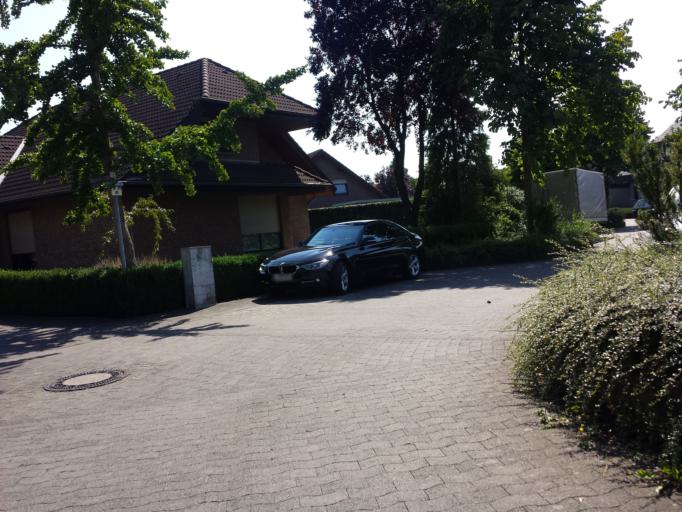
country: DE
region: North Rhine-Westphalia
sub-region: Regierungsbezirk Detmold
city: Guetersloh
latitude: 51.8808
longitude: 8.3784
